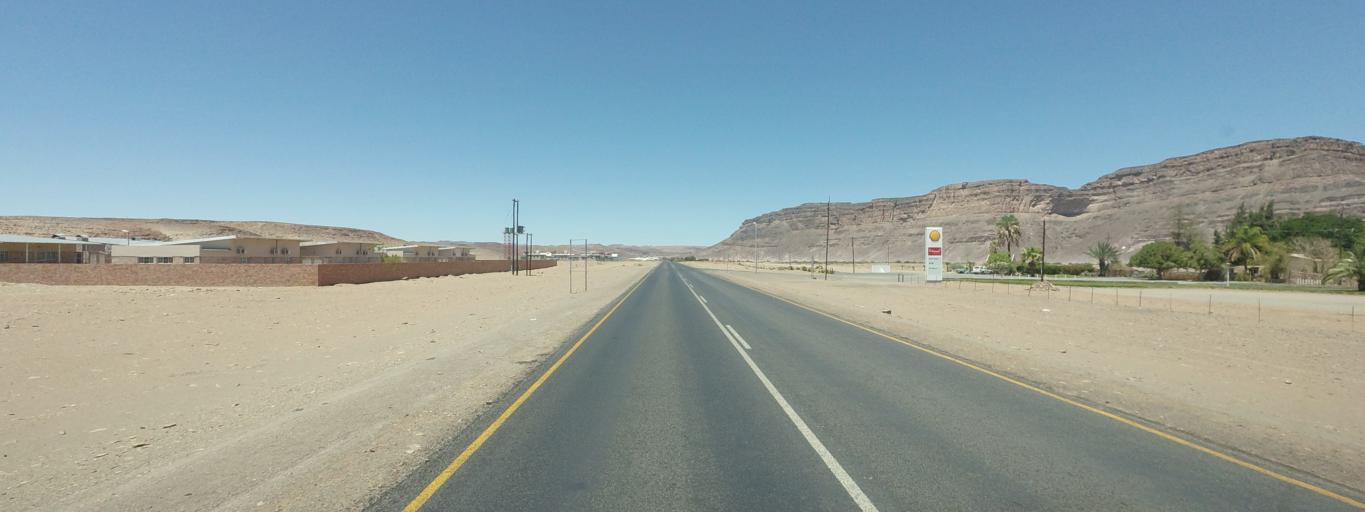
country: ZA
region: Northern Cape
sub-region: Namakwa District Municipality
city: Port Nolloth
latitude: -28.7429
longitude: 17.6175
